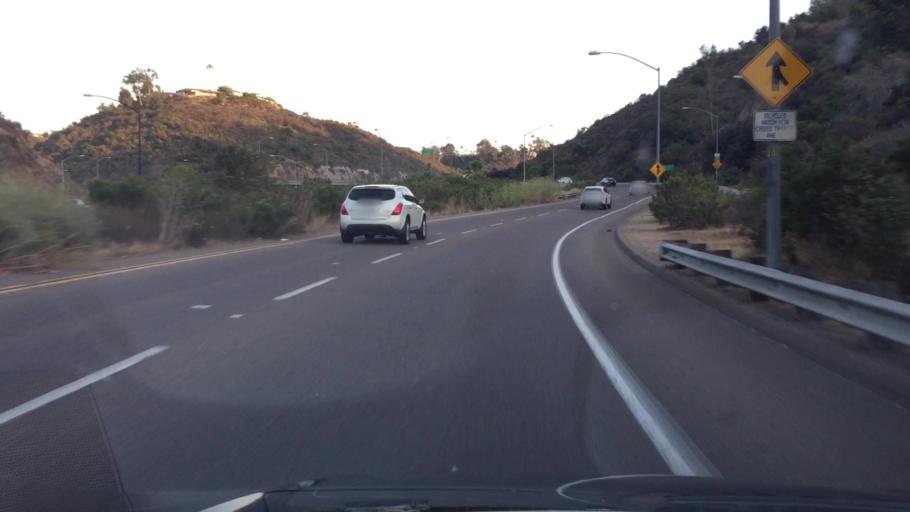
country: US
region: California
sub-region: San Diego County
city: Lemon Grove
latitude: 32.7745
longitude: -117.0983
